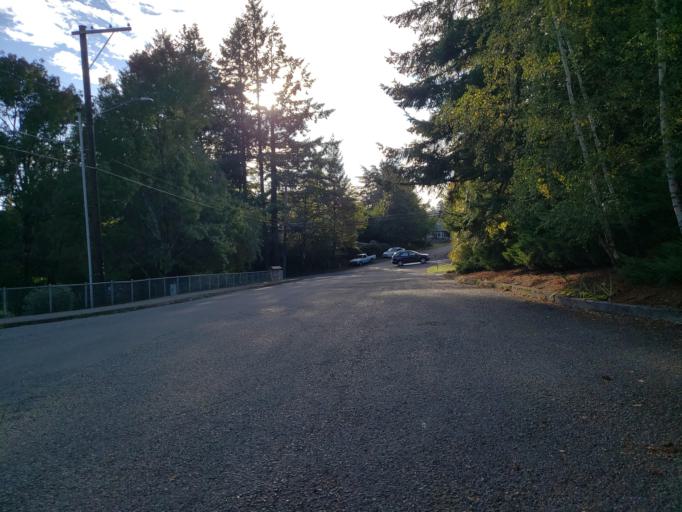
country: US
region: Oregon
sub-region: Multnomah County
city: Portland
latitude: 45.4833
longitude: -122.7072
